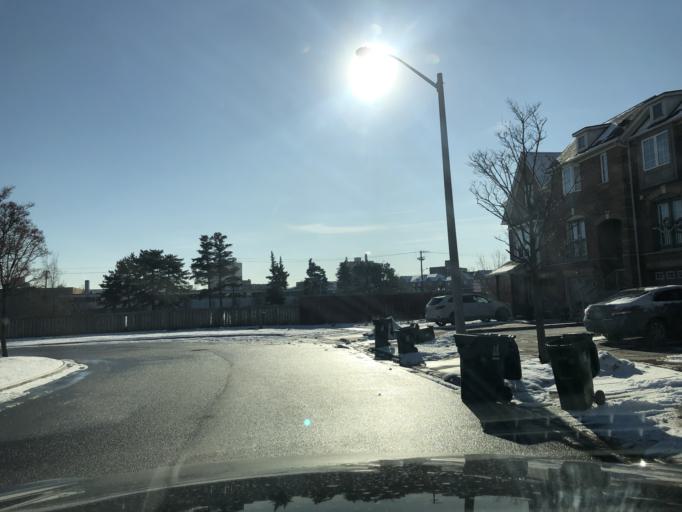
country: CA
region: Ontario
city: Etobicoke
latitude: 43.7097
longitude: -79.5300
